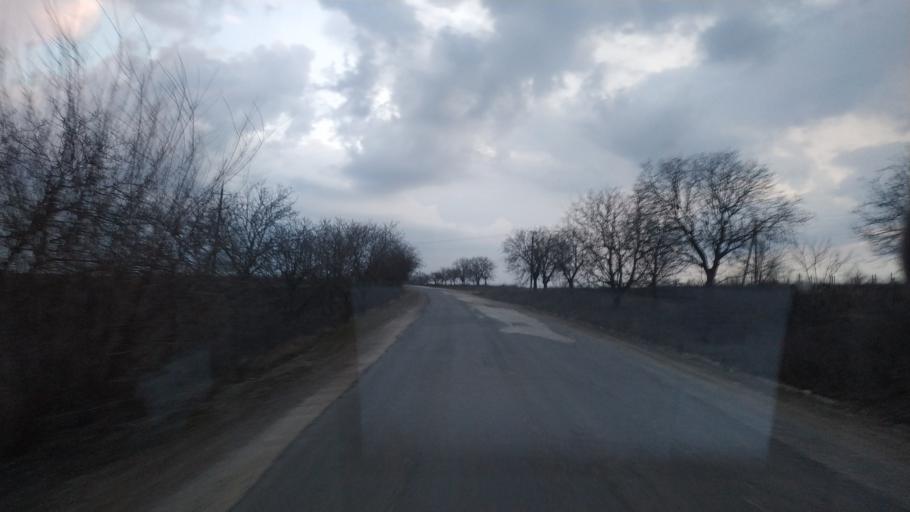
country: MD
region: Anenii Noi
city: Anenii Noi
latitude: 46.9685
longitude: 29.2848
